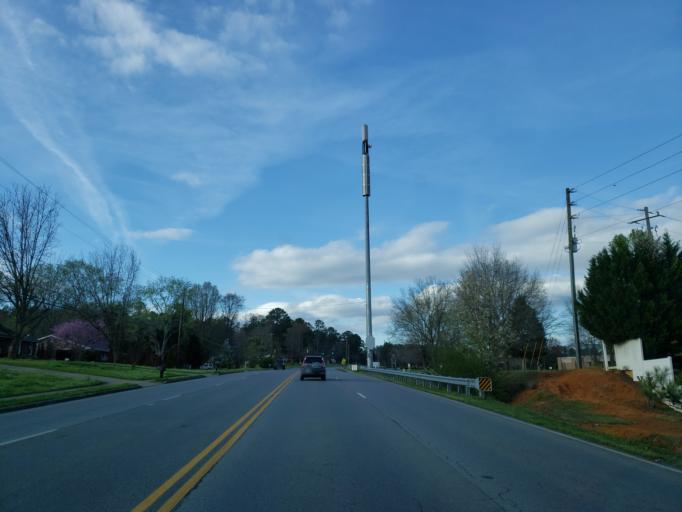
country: US
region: Georgia
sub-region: Bartow County
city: Cartersville
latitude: 34.2234
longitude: -84.8189
